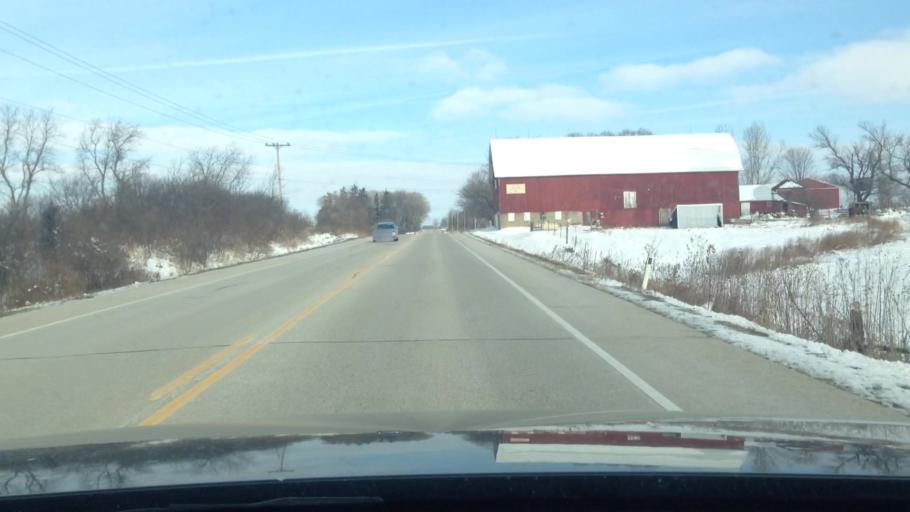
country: US
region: Wisconsin
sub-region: Walworth County
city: Lake Geneva
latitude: 42.6574
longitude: -88.4137
